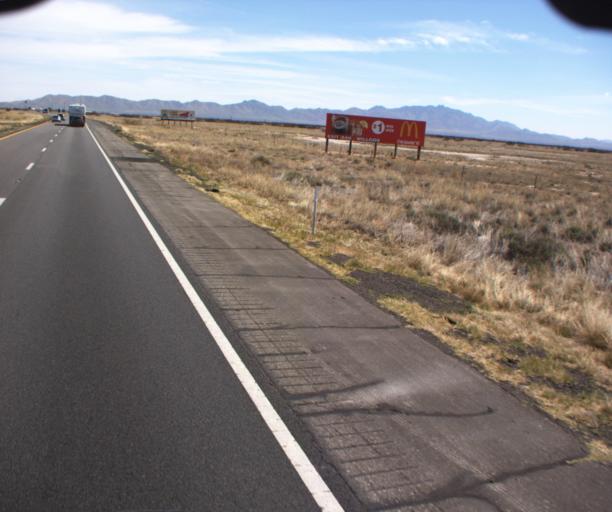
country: US
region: Arizona
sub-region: Cochise County
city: Willcox
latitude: 32.2133
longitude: -109.8873
